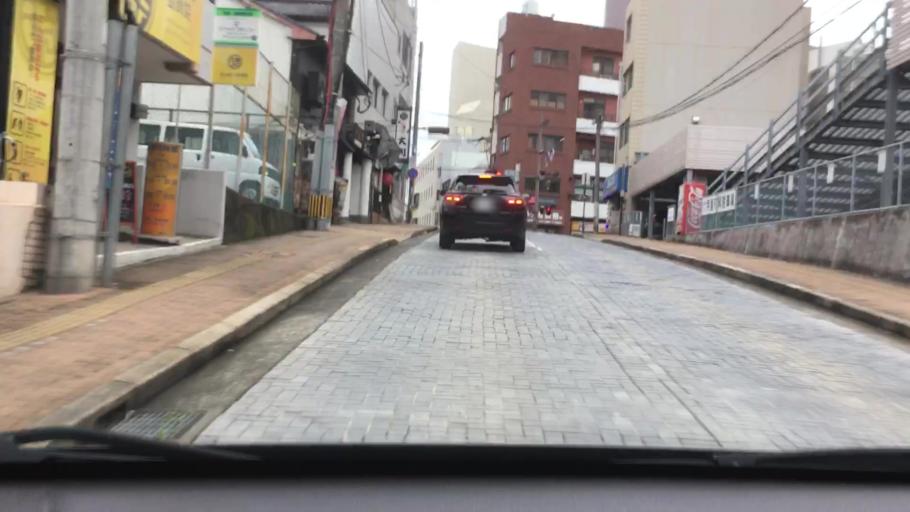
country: JP
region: Nagasaki
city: Nagasaki-shi
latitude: 32.7501
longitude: 129.8766
